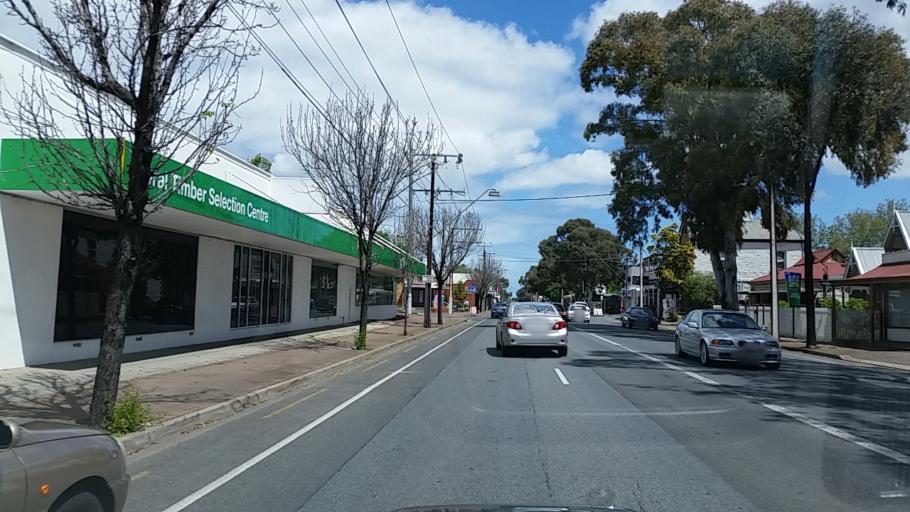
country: AU
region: South Australia
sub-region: Norwood Payneham St Peters
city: Trinity Gardens
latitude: -34.9150
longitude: 138.6370
